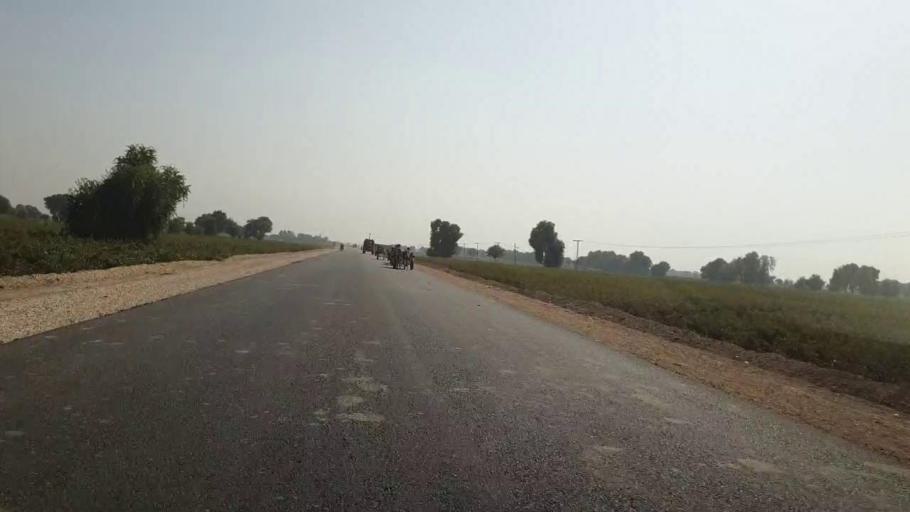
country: PK
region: Sindh
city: Dadu
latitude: 26.6703
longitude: 67.7765
